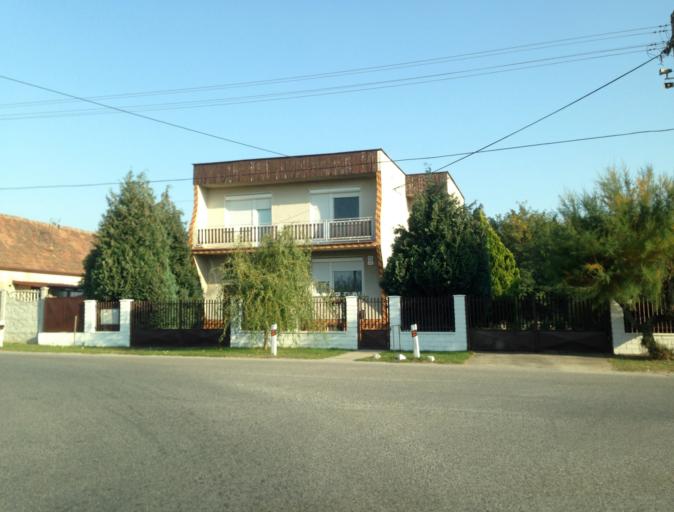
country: SK
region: Nitriansky
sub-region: Okres Komarno
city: Hurbanovo
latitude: 47.8884
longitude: 18.2065
